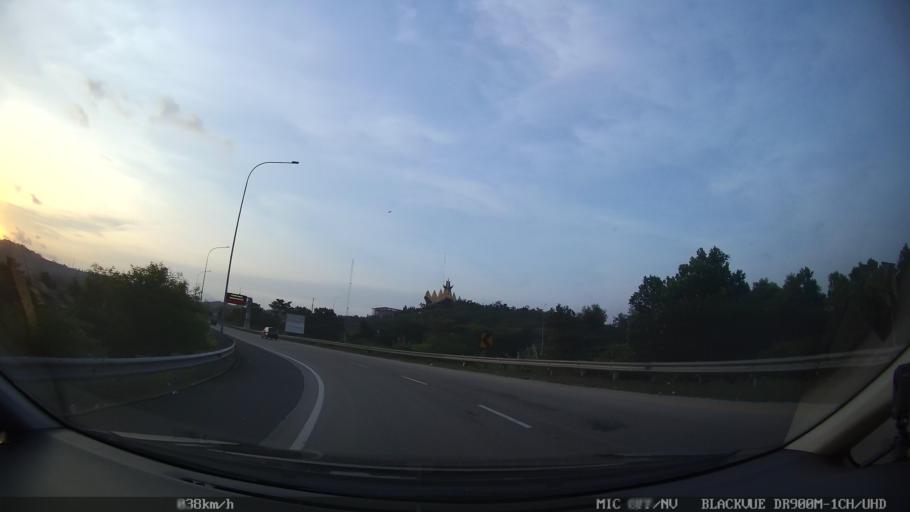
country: ID
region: Lampung
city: Penengahan
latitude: -5.8696
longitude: 105.7510
